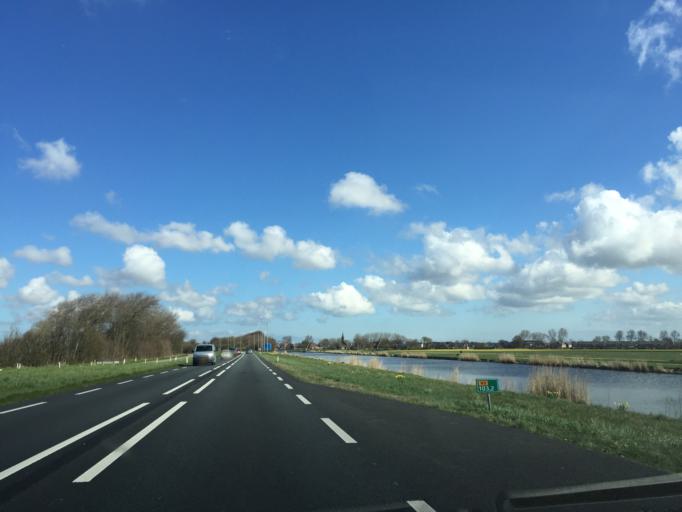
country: NL
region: North Holland
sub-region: Gemeente Schagen
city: Schagen
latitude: 52.8290
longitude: 4.7484
